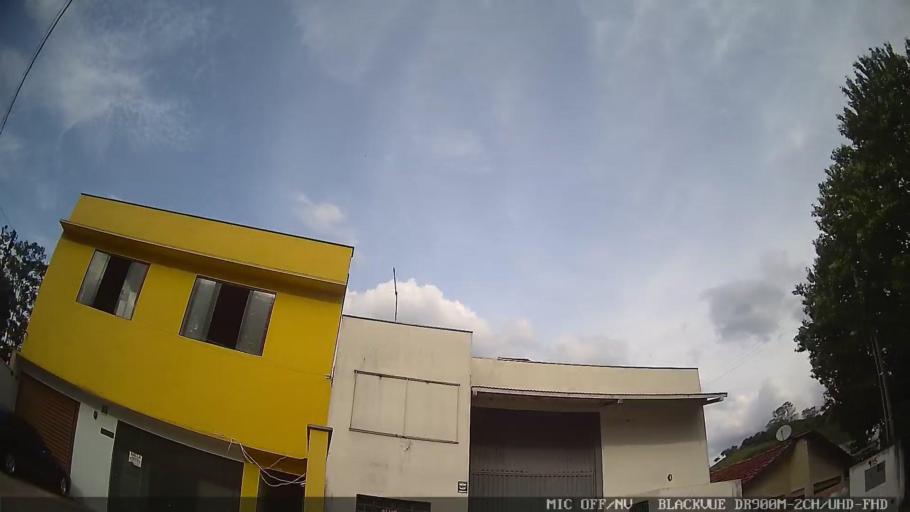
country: BR
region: Sao Paulo
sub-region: Amparo
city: Amparo
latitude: -22.7190
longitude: -46.7717
